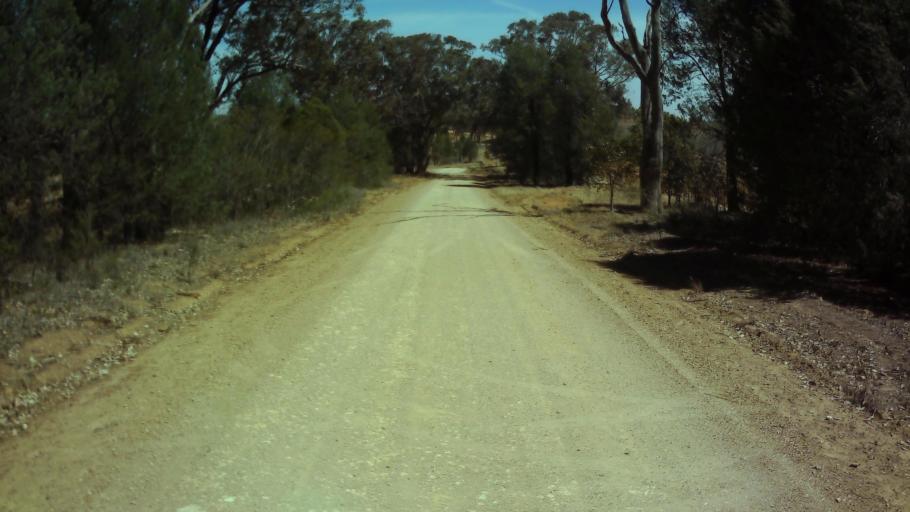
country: AU
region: New South Wales
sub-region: Weddin
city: Grenfell
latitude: -33.9208
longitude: 148.1786
